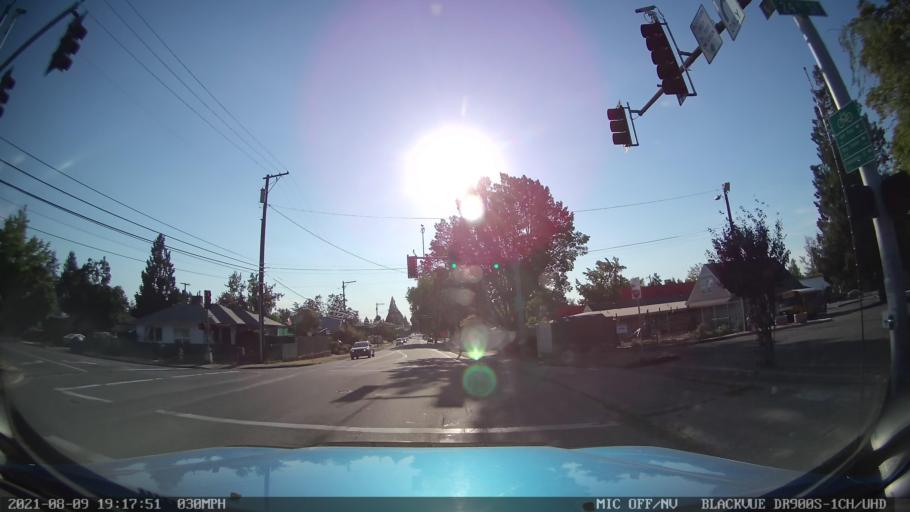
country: US
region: Oregon
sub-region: Marion County
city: Salem
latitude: 44.9401
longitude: -123.0084
